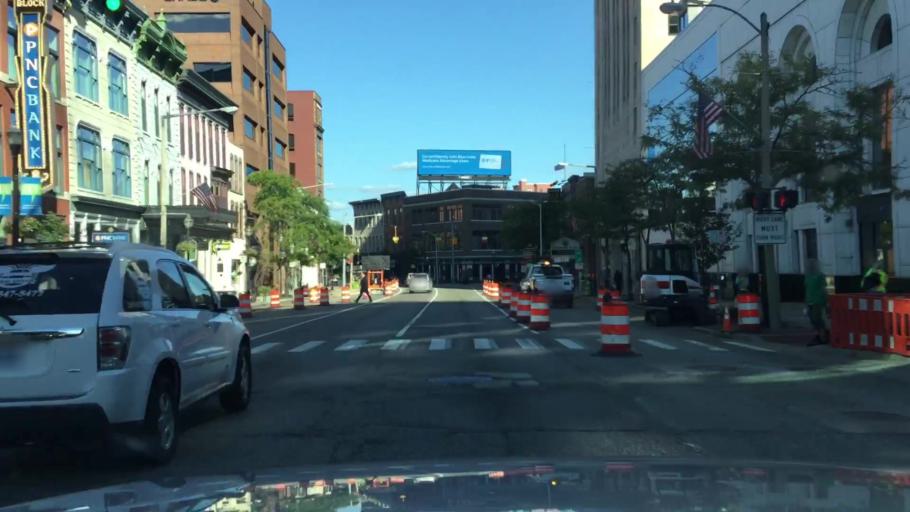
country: US
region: Michigan
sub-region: Kalamazoo County
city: Kalamazoo
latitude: 42.2917
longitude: -85.5834
